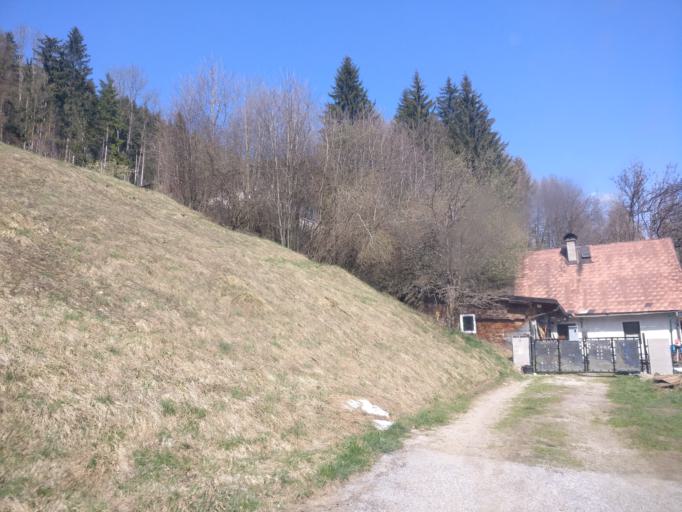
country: AT
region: Salzburg
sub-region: Politischer Bezirk Sankt Johann im Pongau
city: Bischofshofen
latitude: 47.4235
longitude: 13.2133
